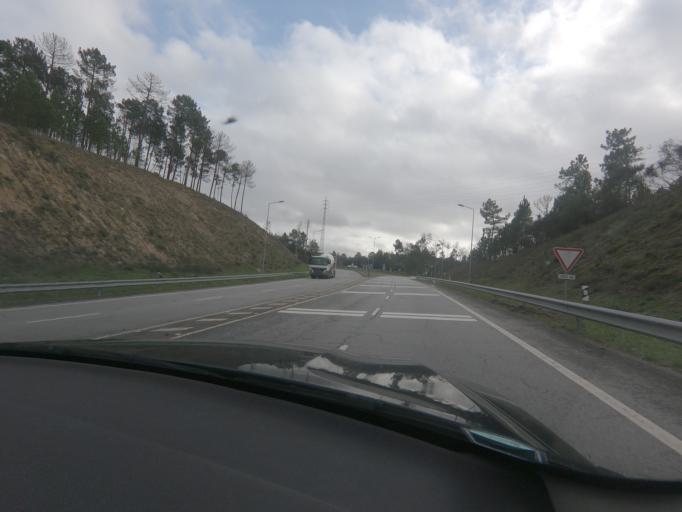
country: PT
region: Viseu
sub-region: Viseu
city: Campo
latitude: 40.7043
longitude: -7.9435
